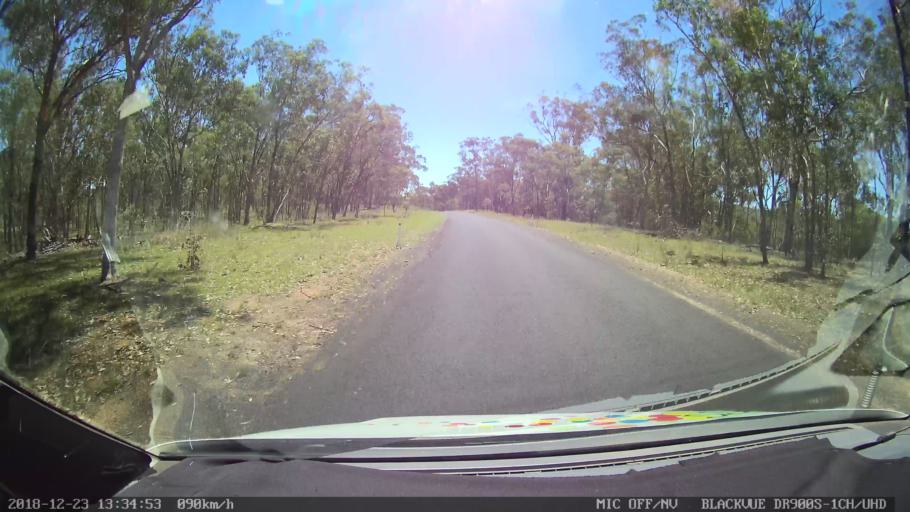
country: AU
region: New South Wales
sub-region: Armidale Dumaresq
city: Armidale
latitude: -30.4443
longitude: 151.2610
